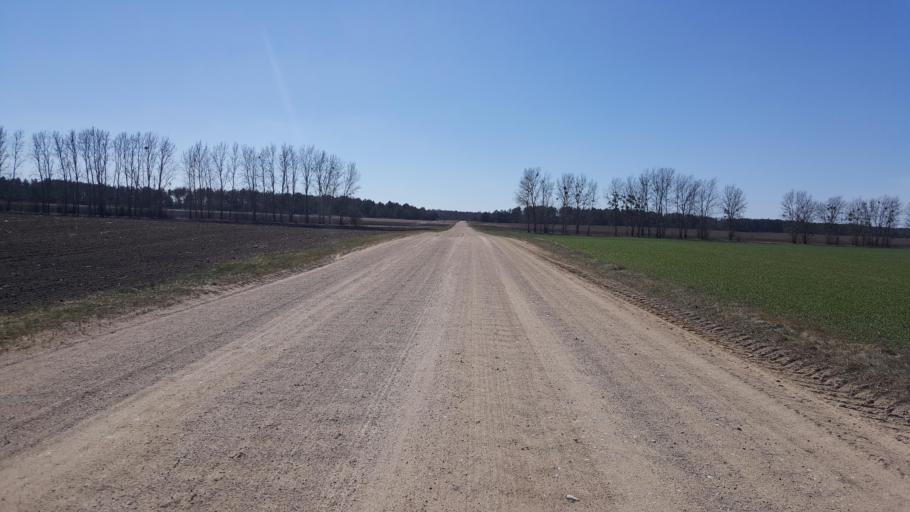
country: BY
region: Brest
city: Kamyanyets
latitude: 52.3130
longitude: 23.8615
